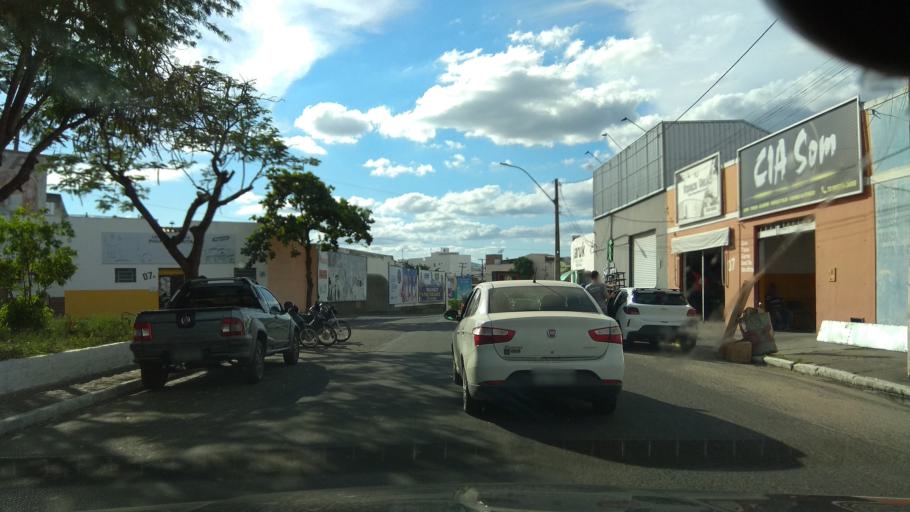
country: BR
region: Bahia
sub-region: Jequie
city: Jequie
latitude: -13.8658
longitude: -40.0770
